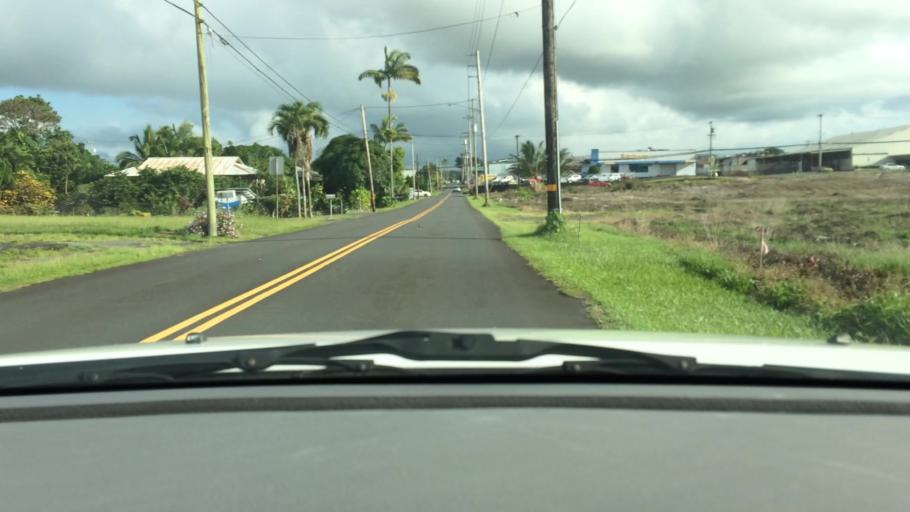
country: US
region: Hawaii
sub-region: Hawaii County
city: Hilo
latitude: 19.7133
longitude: -155.0714
